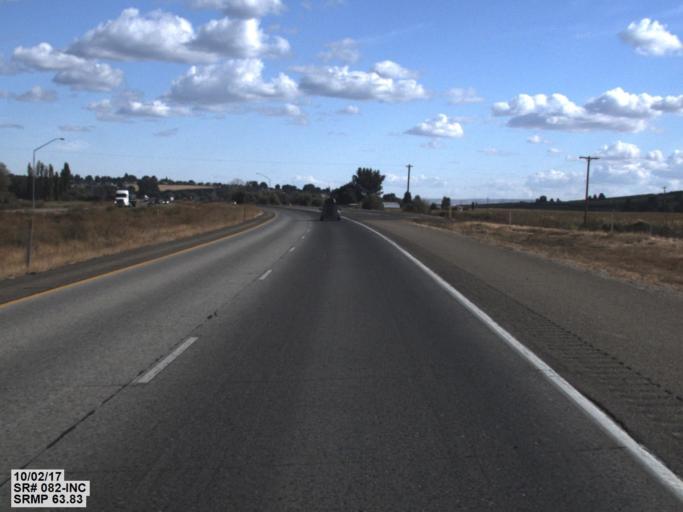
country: US
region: Washington
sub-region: Yakima County
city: Sunnyside
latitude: 46.3246
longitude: -120.0752
